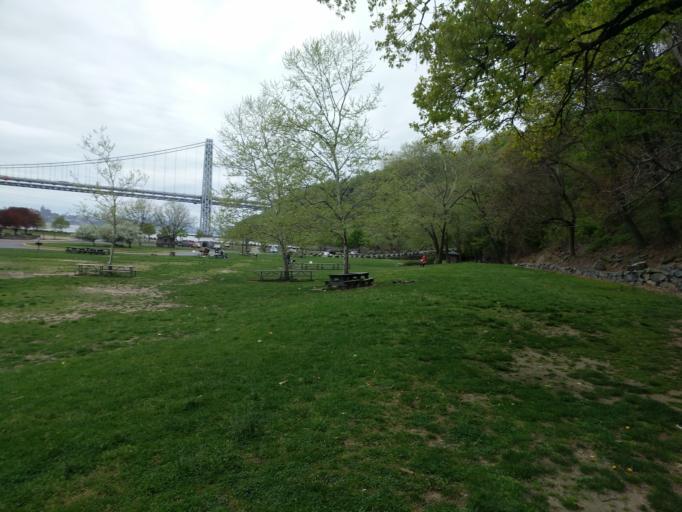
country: US
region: New Jersey
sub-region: Bergen County
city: Fort Lee
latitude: 40.8616
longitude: -73.9555
